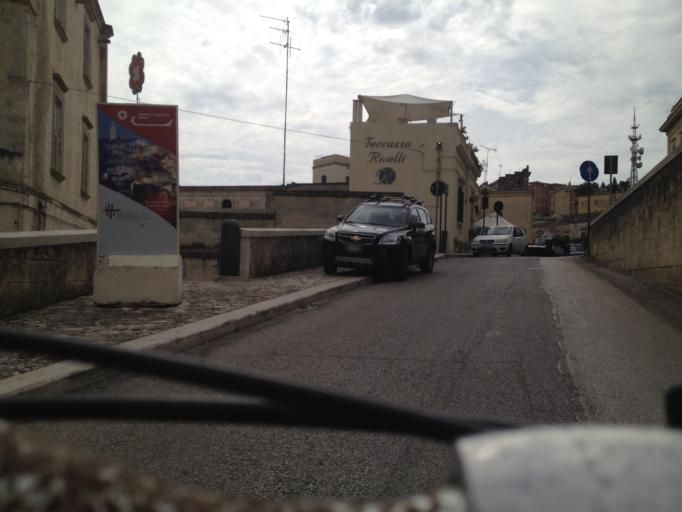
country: IT
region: Basilicate
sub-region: Provincia di Matera
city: Matera
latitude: 40.6629
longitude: 16.6101
